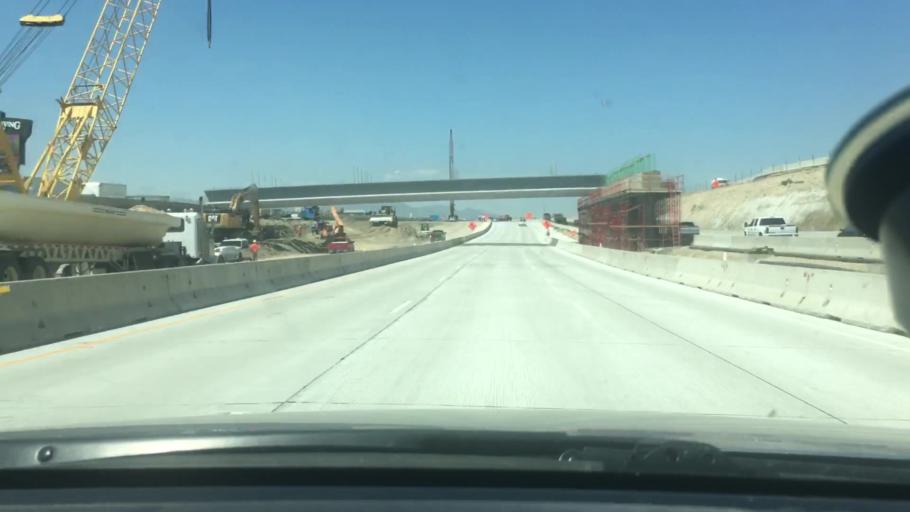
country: US
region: Utah
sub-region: Utah County
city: Lehi
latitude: 40.4236
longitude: -111.8821
